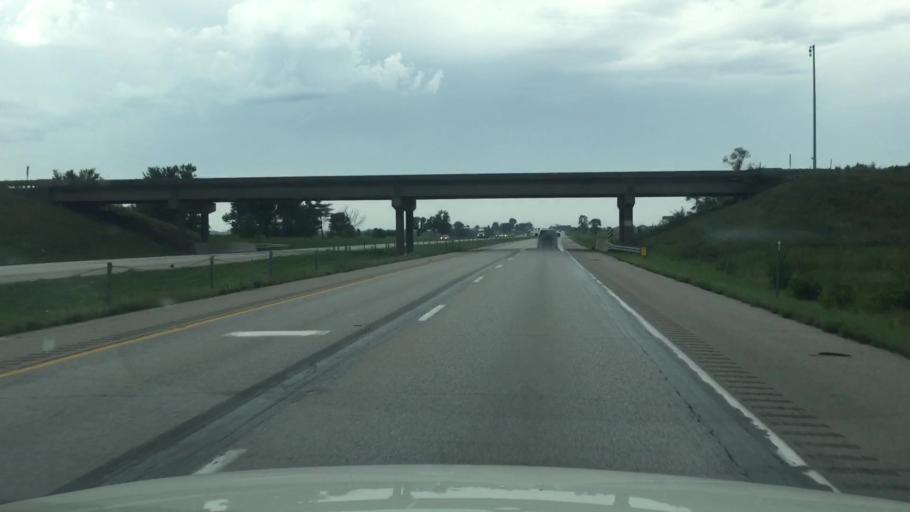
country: US
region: Iowa
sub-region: Polk County
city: Ankeny
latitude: 41.7920
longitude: -93.5706
